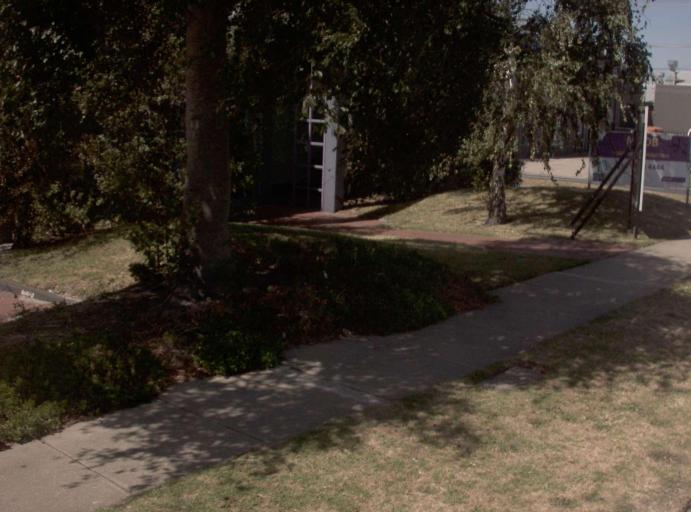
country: AU
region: Victoria
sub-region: Bayside
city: Highett
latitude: -37.9551
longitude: 145.0320
